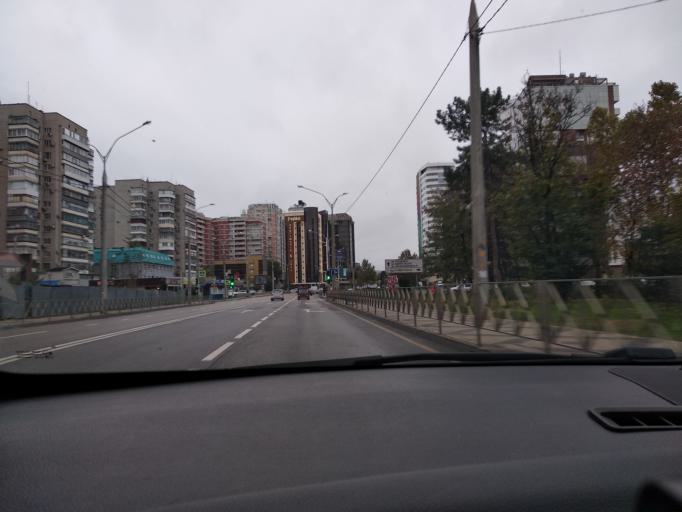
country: RU
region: Krasnodarskiy
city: Krasnodar
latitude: 45.0202
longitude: 38.9598
